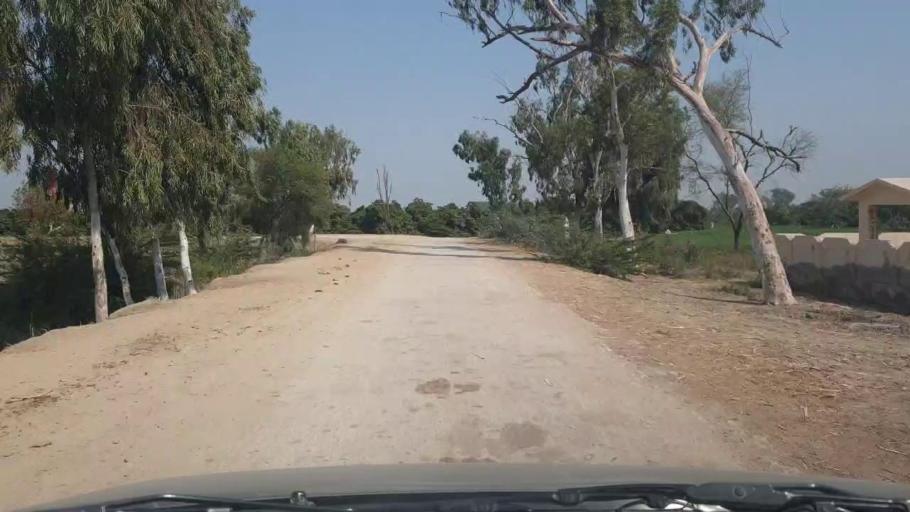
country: PK
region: Sindh
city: Mirwah Gorchani
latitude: 25.3594
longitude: 69.1443
